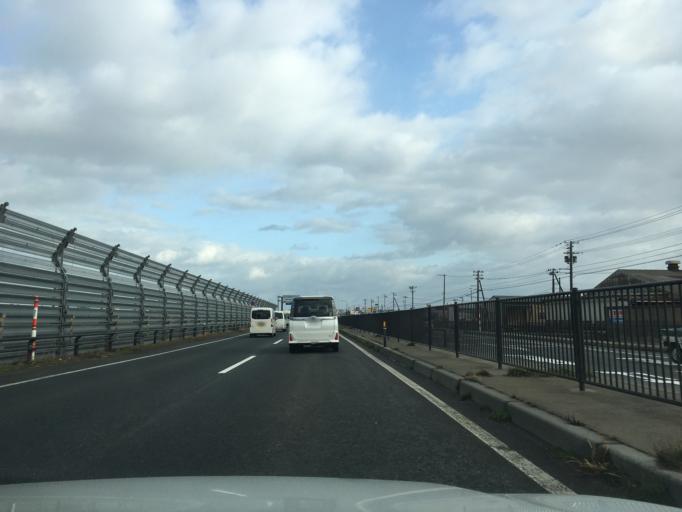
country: JP
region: Yamagata
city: Sakata
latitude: 38.8627
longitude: 139.8440
